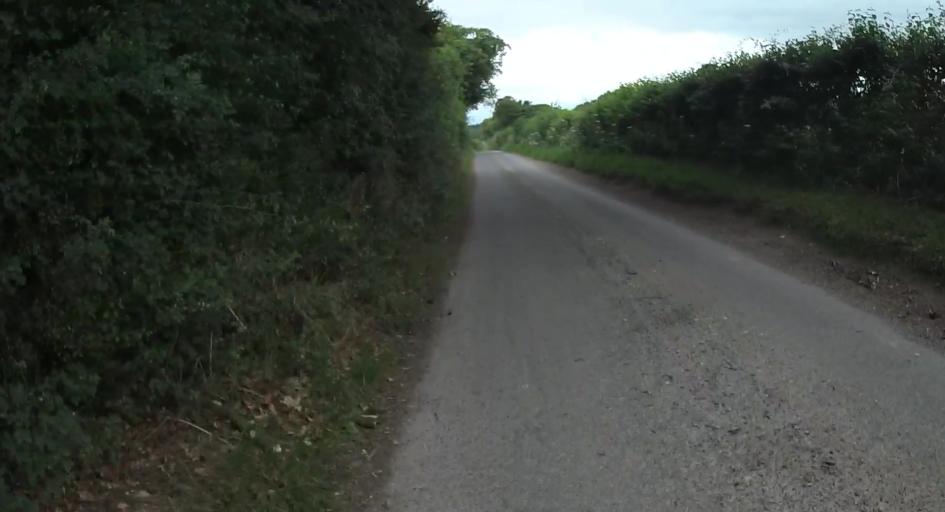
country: GB
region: England
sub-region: Hampshire
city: Four Marks
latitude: 51.0607
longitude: -1.1546
